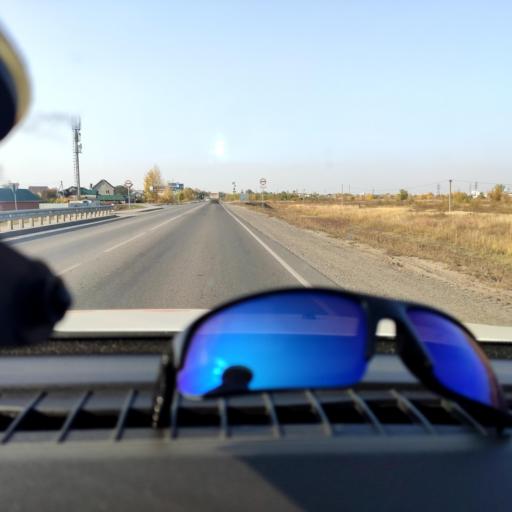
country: RU
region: Samara
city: Samara
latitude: 53.1213
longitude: 50.1185
